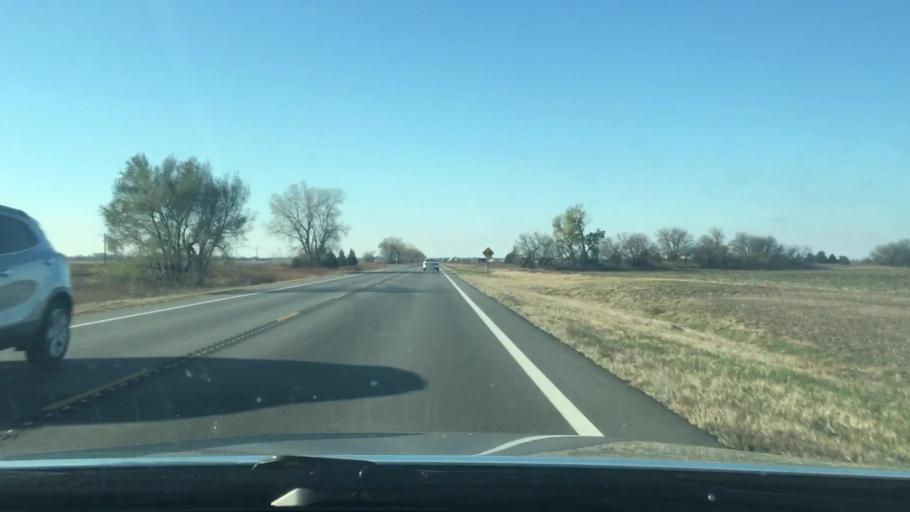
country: US
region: Kansas
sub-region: Reno County
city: Nickerson
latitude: 38.1225
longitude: -98.0473
